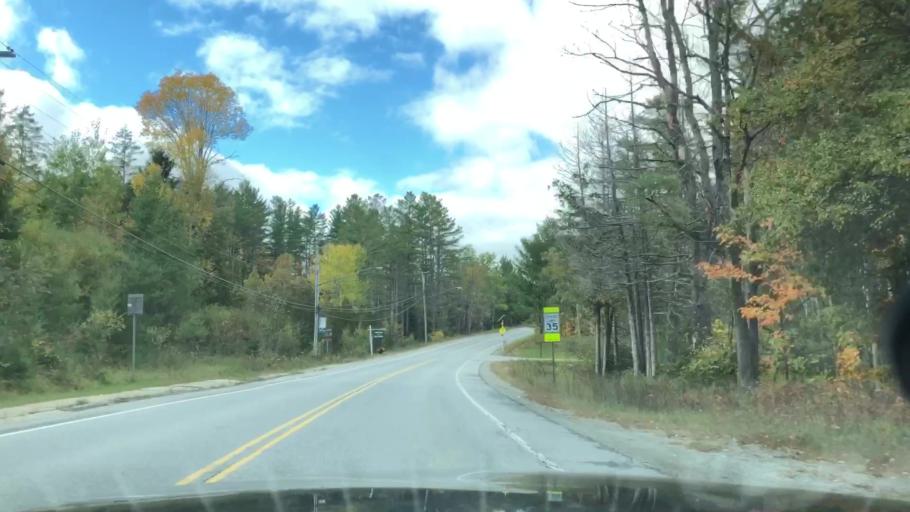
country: US
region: New York
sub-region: Essex County
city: Lake Placid
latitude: 43.9696
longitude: -74.1468
